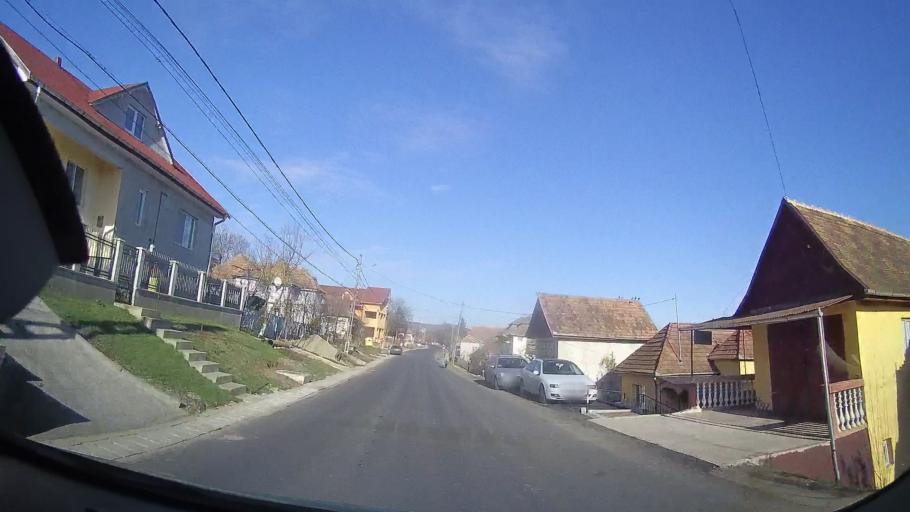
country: RO
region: Mures
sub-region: Comuna Zau De Campie
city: Zau de Campie
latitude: 46.6102
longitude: 24.1232
